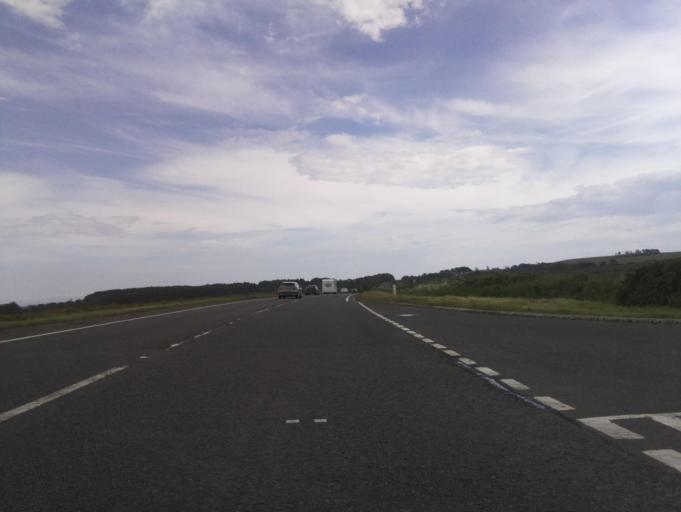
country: GB
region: England
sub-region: Northumberland
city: Ellingham
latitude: 55.5264
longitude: -1.7566
